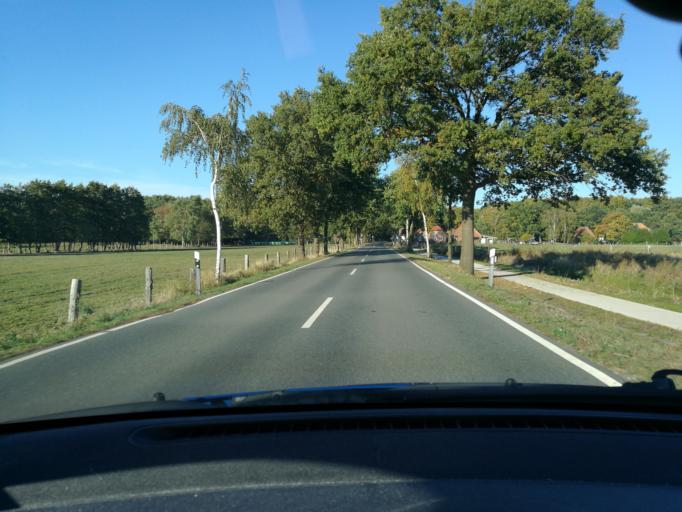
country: DE
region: Lower Saxony
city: Rullstorf
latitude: 53.2945
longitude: 10.5580
